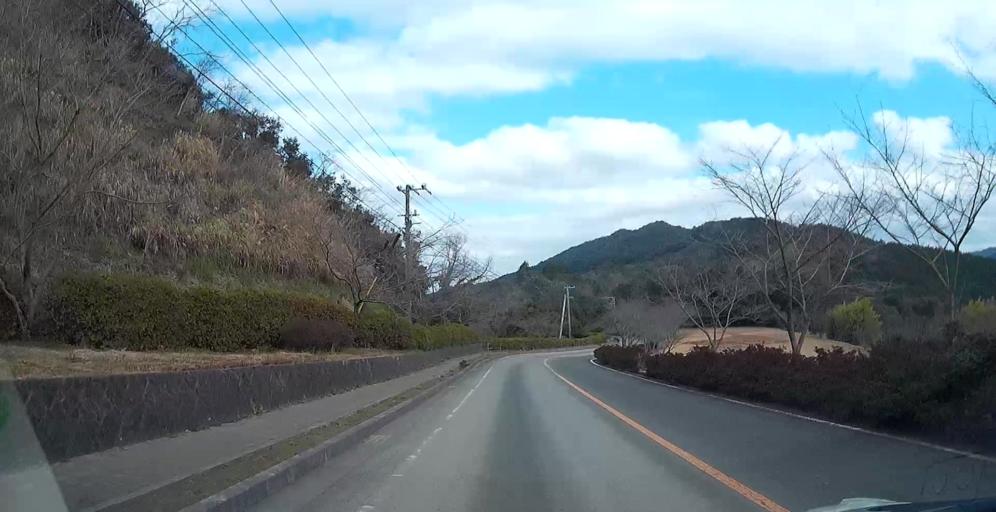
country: JP
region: Kumamoto
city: Yatsushiro
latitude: 32.3712
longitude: 130.5016
